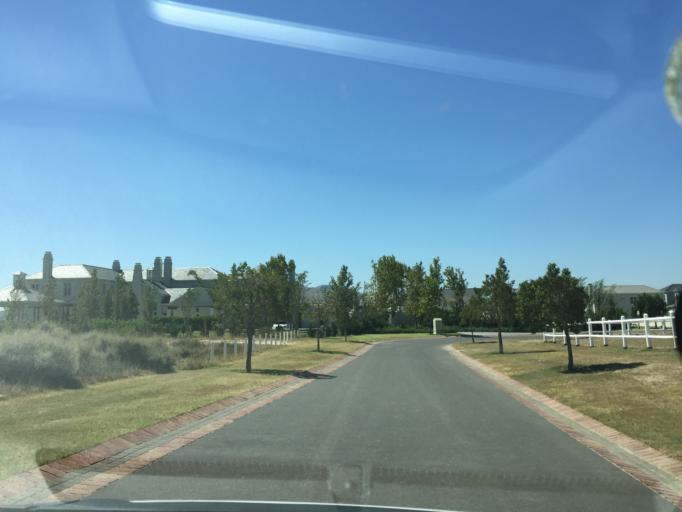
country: ZA
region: Western Cape
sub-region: Cape Winelands District Municipality
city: Paarl
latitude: -33.8066
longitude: 18.9767
